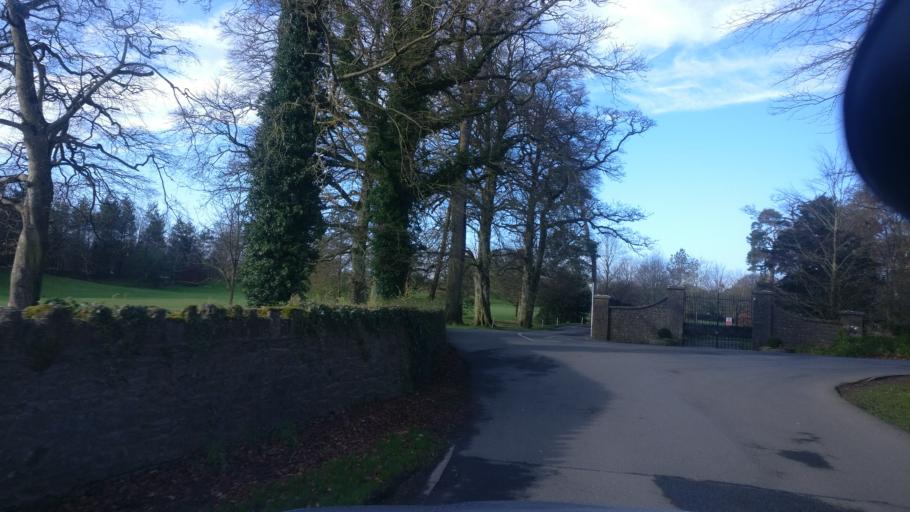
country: IE
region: Leinster
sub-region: Kilkenny
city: Thomastown
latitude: 52.5262
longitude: -7.1908
